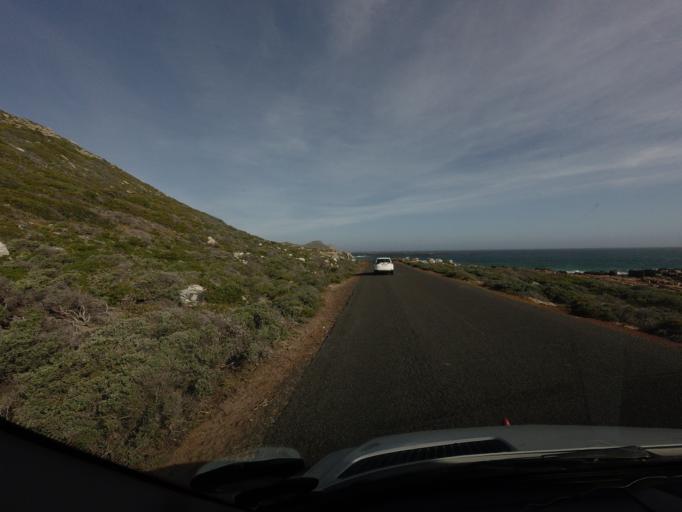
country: ZA
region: Western Cape
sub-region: City of Cape Town
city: Retreat
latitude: -34.3449
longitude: 18.4626
